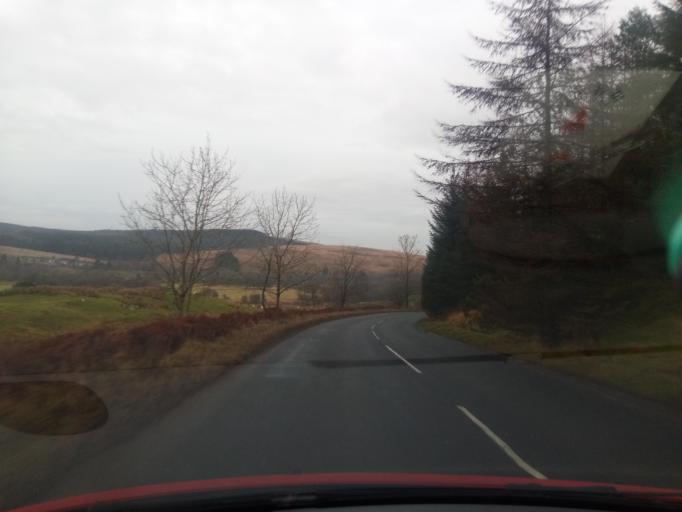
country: GB
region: England
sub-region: Northumberland
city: Haltwhistle
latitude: 55.1778
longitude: -2.4490
